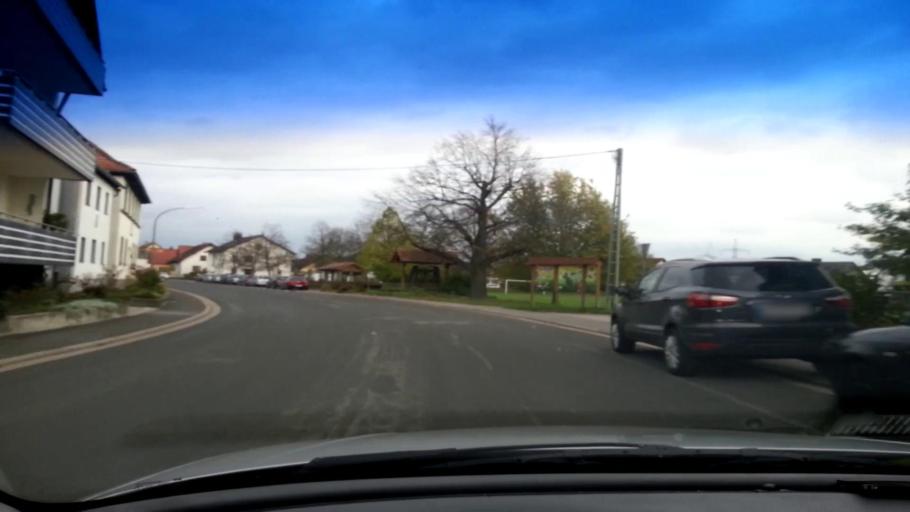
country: DE
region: Bavaria
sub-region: Upper Franconia
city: Viereth-Trunstadt
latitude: 49.9353
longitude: 10.7887
